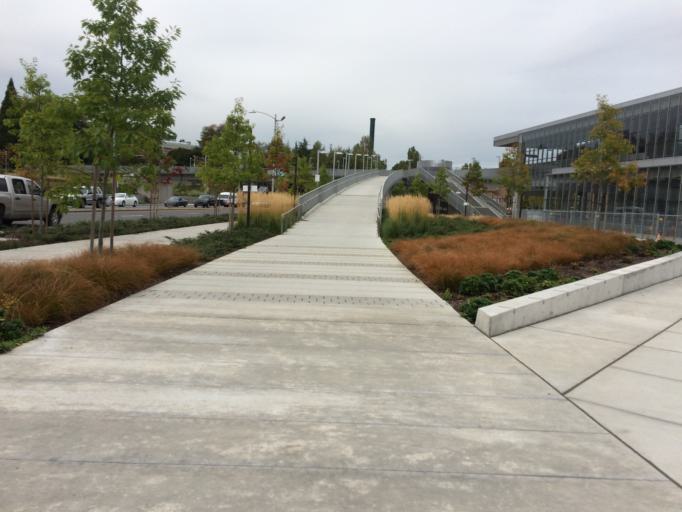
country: US
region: Washington
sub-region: King County
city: Seattle
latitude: 47.6493
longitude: -122.3043
